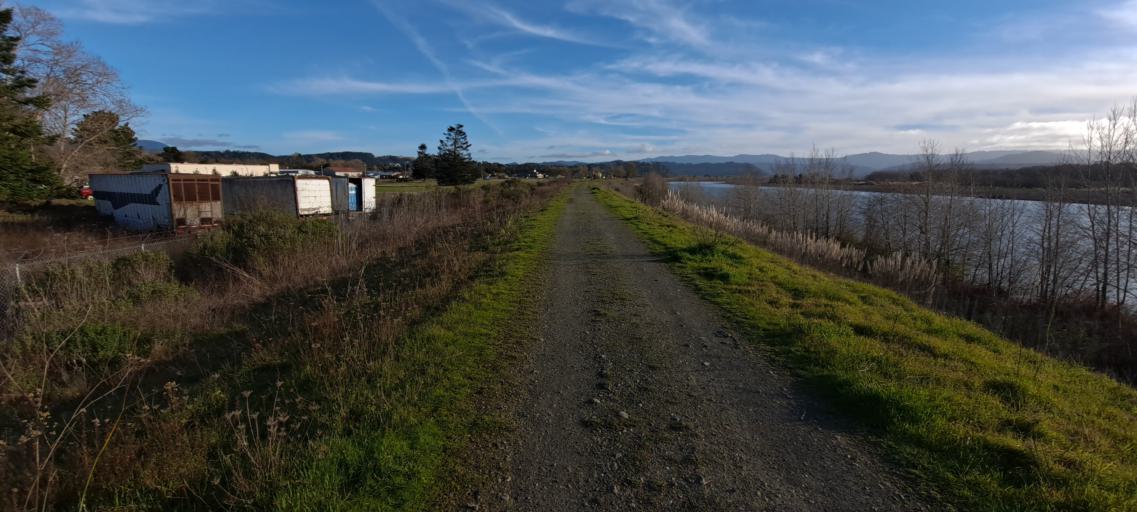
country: US
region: California
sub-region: Humboldt County
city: Fortuna
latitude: 40.5845
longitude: -124.1584
